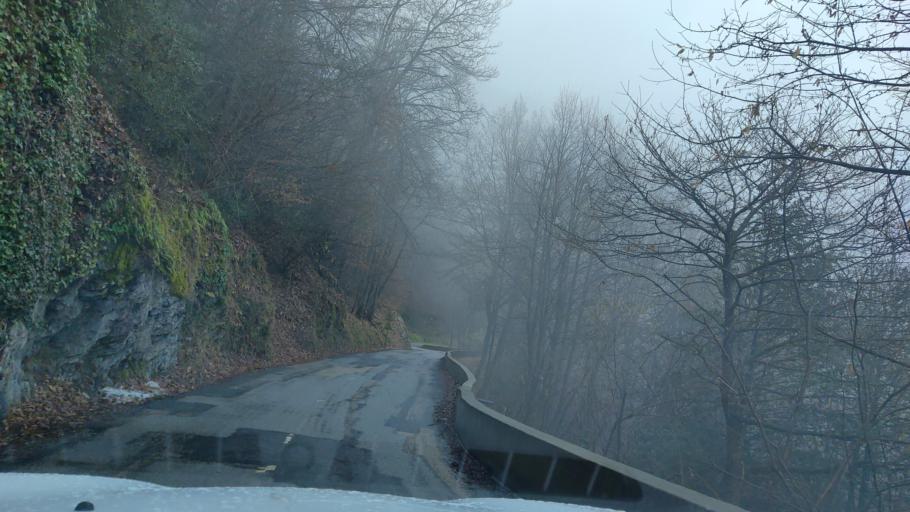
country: FR
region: Rhone-Alpes
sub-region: Departement de la Savoie
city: Aiton
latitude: 45.5179
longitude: 6.3042
